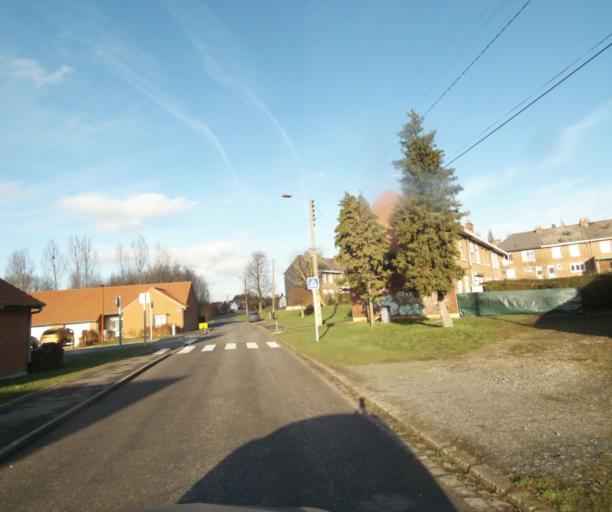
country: FR
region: Nord-Pas-de-Calais
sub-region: Departement du Nord
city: Marly
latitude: 50.3424
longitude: 3.5447
